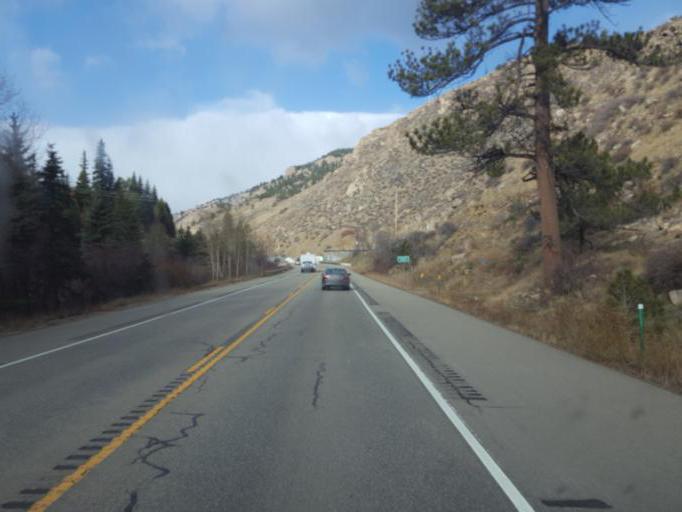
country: US
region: Colorado
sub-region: Clear Creek County
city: Georgetown
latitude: 39.4610
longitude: -105.6729
